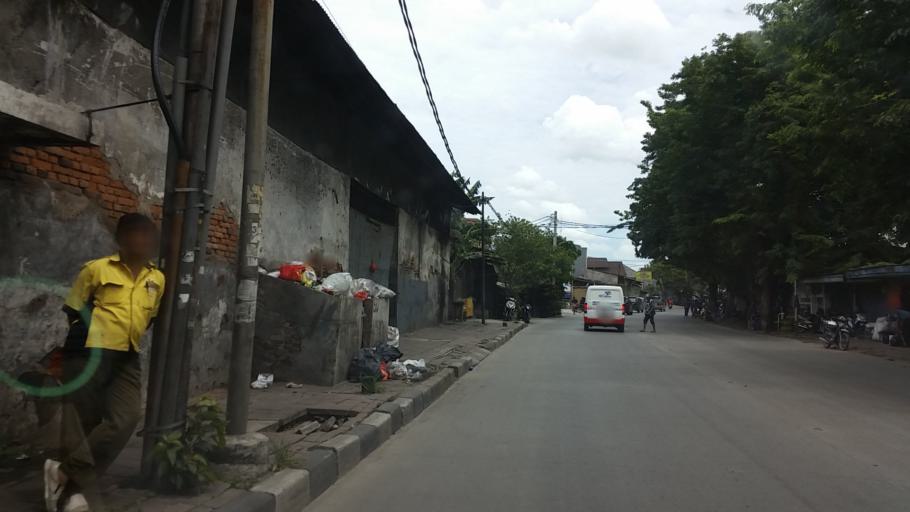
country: ID
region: Jakarta Raya
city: Jakarta
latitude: -6.1259
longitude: 106.8102
